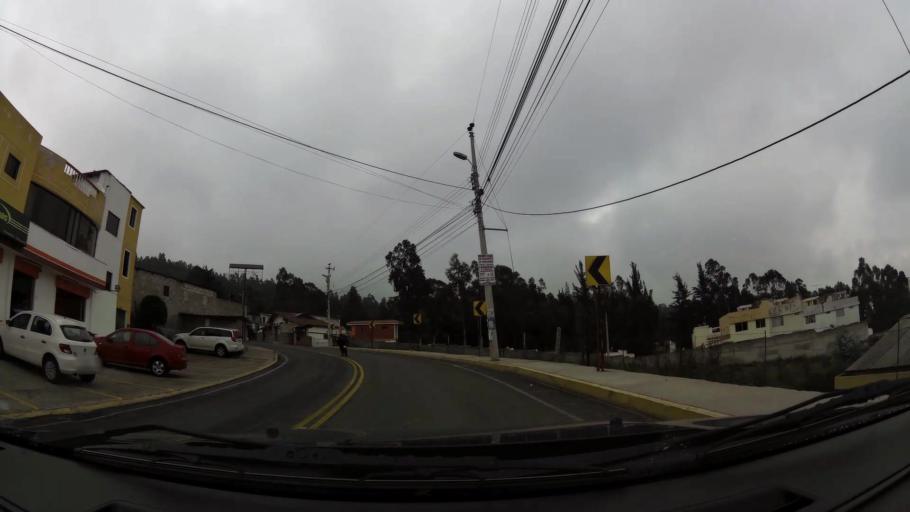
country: EC
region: Pichincha
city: Quito
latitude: -0.2628
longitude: -78.4806
